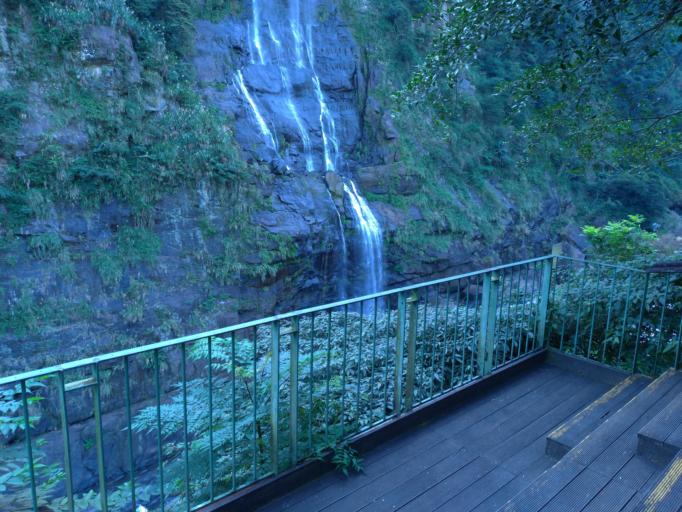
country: TW
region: Taipei
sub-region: Taipei
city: Banqiao
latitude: 24.8484
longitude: 121.5519
